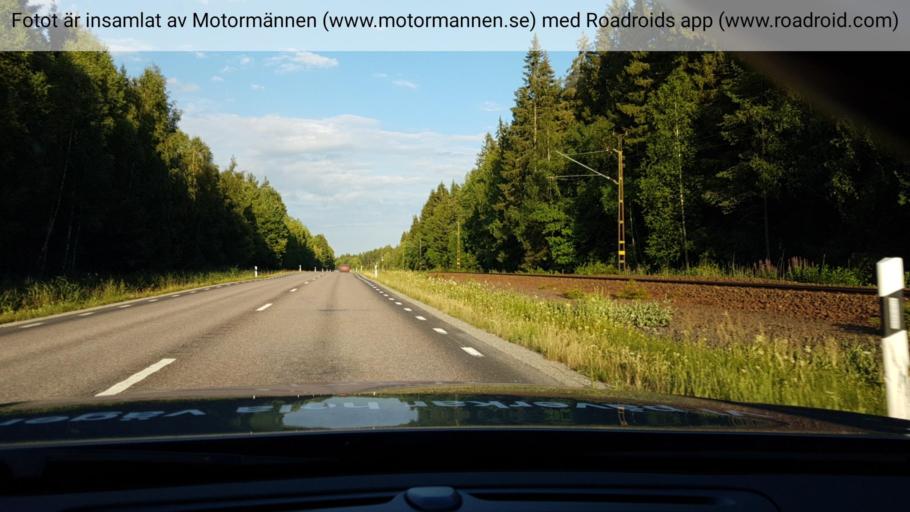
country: SE
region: Uppsala
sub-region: Enkopings Kommun
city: Orsundsbro
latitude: 59.8825
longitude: 17.2256
